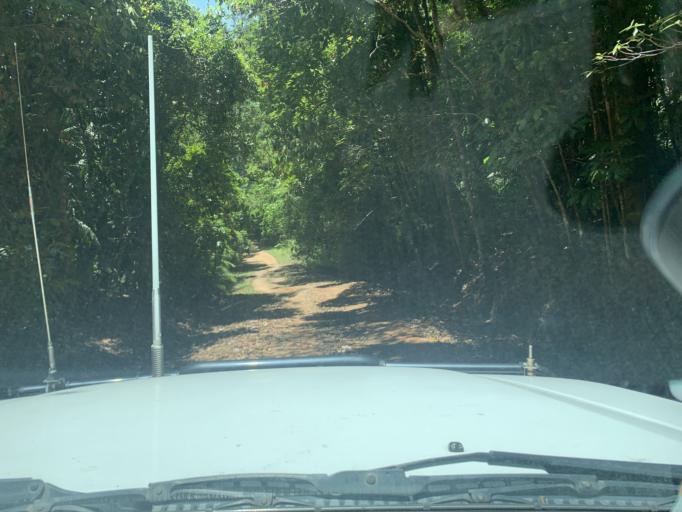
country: AU
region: Queensland
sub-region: Cairns
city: Woree
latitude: -16.9735
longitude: 145.6503
